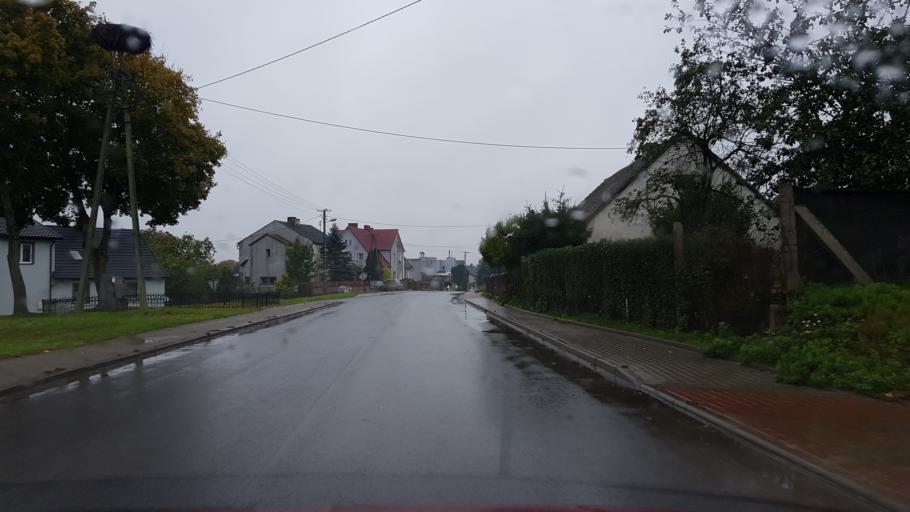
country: PL
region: Greater Poland Voivodeship
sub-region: Powiat zlotowski
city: Tarnowka
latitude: 53.3421
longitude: 16.8411
